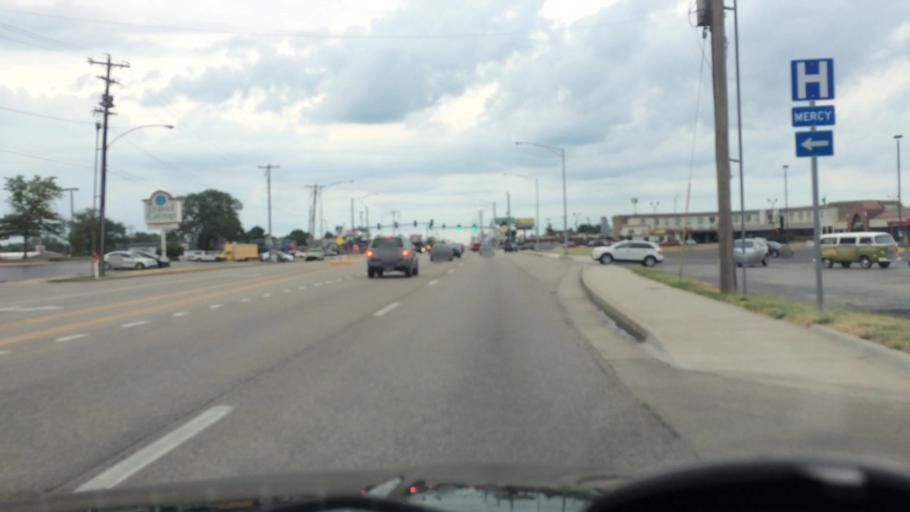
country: US
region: Missouri
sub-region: Greene County
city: Springfield
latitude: 37.1799
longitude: -93.2623
